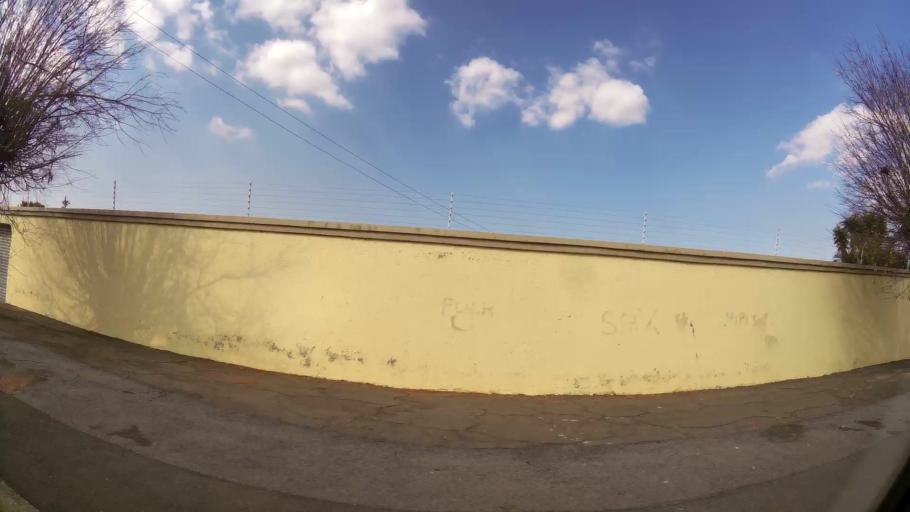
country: ZA
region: Gauteng
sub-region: Ekurhuleni Metropolitan Municipality
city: Germiston
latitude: -26.1788
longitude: 28.1803
